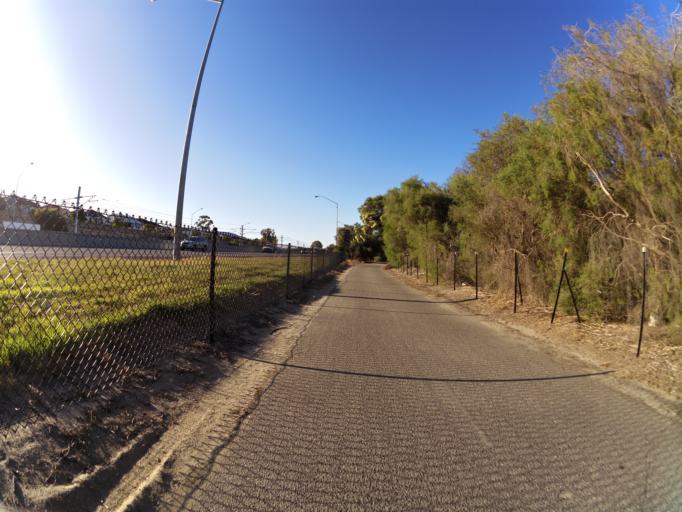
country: AU
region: Western Australia
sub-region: South Perth
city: Manning
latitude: -32.0178
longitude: 115.8572
